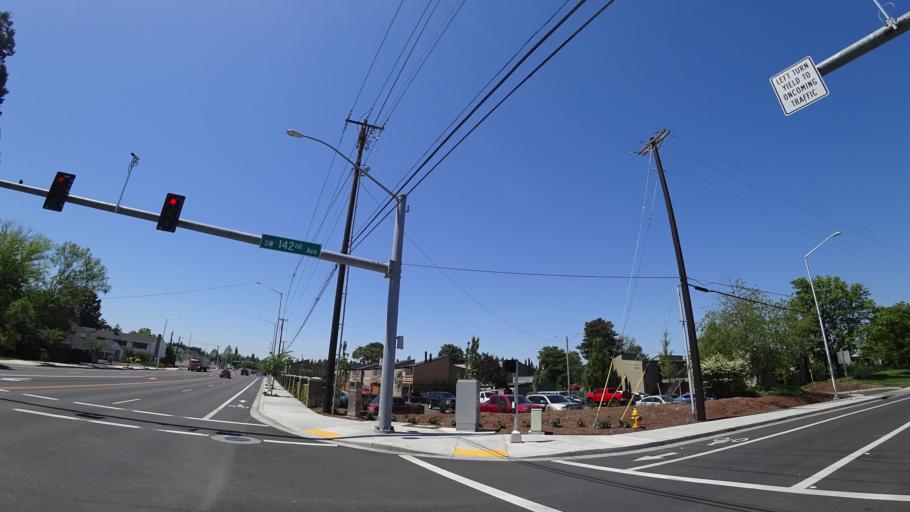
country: US
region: Oregon
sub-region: Washington County
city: Beaverton
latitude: 45.4864
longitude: -122.8224
